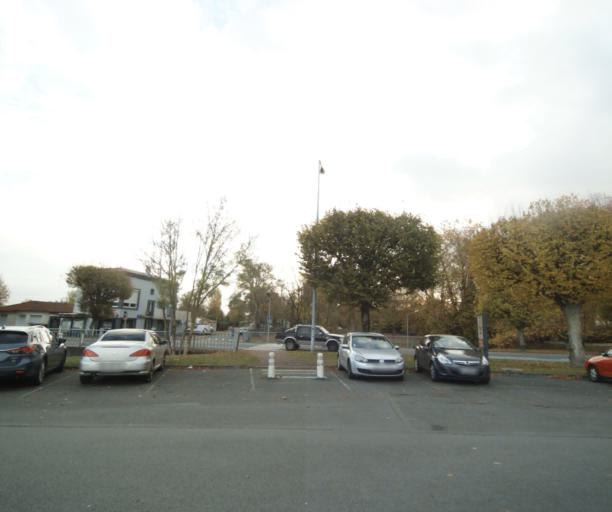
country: FR
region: Poitou-Charentes
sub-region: Departement de la Charente-Maritime
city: Saintes
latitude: 45.7524
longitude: -0.6510
